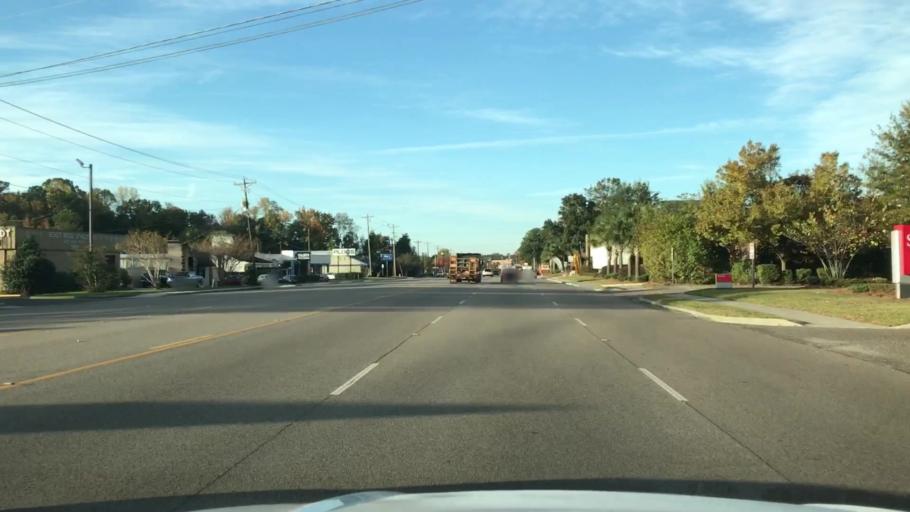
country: US
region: South Carolina
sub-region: Charleston County
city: North Charleston
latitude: 32.7996
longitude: -80.0211
